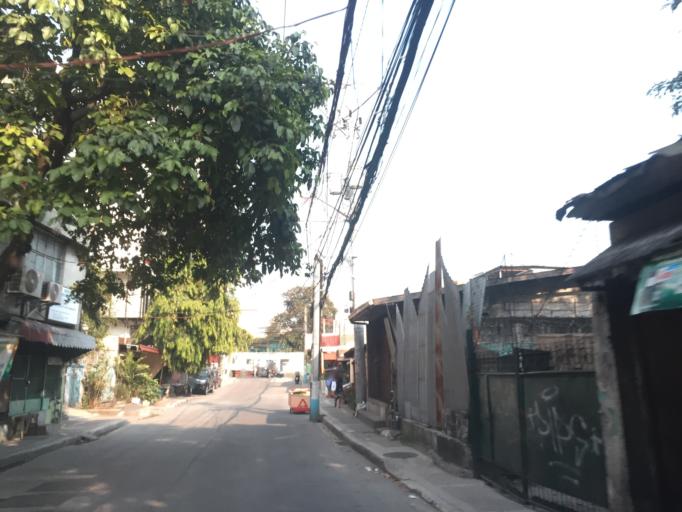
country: PH
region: Calabarzon
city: Bagong Pagasa
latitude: 14.6631
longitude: 121.0198
